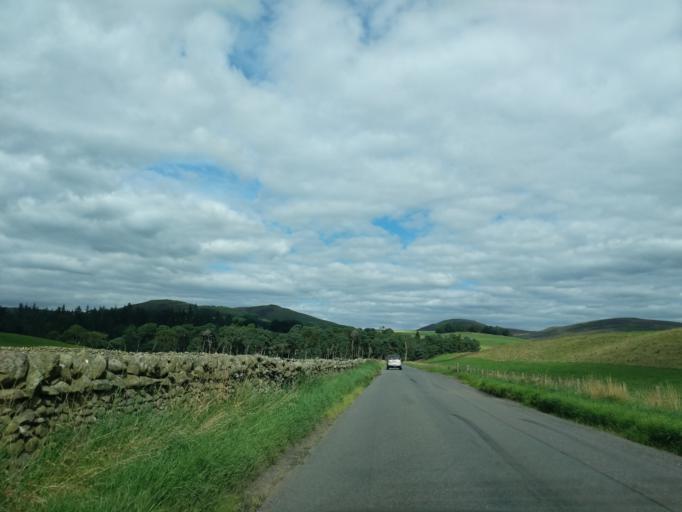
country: GB
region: Scotland
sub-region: The Scottish Borders
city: Peebles
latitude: 55.6475
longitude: -3.2752
